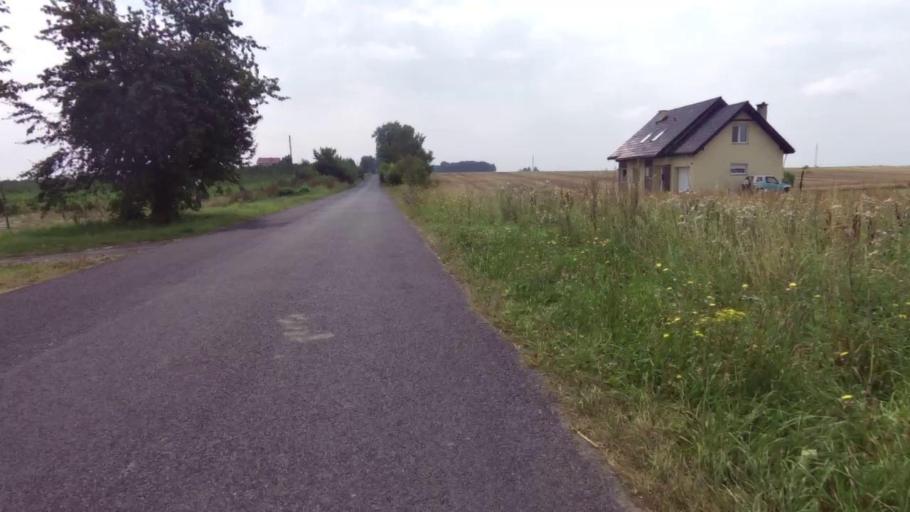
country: PL
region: West Pomeranian Voivodeship
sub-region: Powiat choszczenski
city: Choszczno
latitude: 53.2007
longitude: 15.3926
